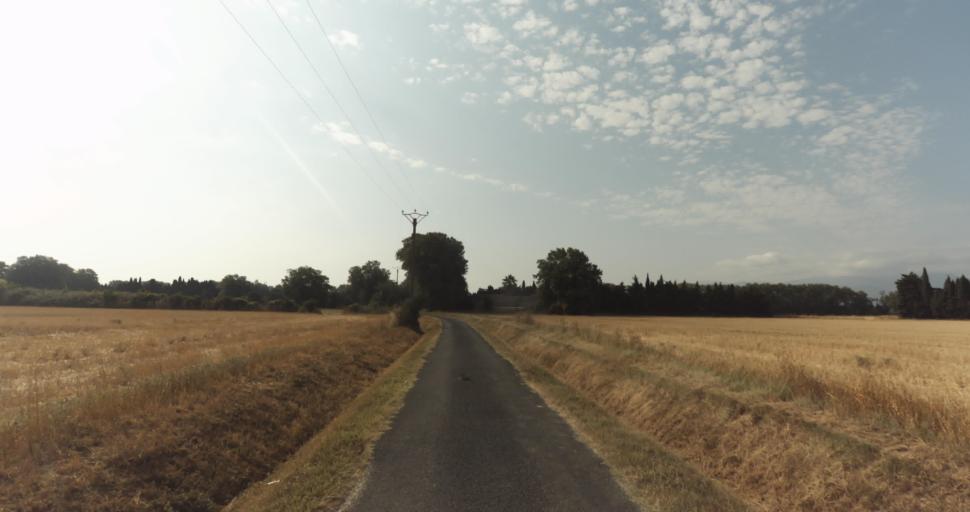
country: FR
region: Languedoc-Roussillon
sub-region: Departement des Pyrenees-Orientales
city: Latour-Bas-Elne
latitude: 42.6092
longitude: 3.0147
